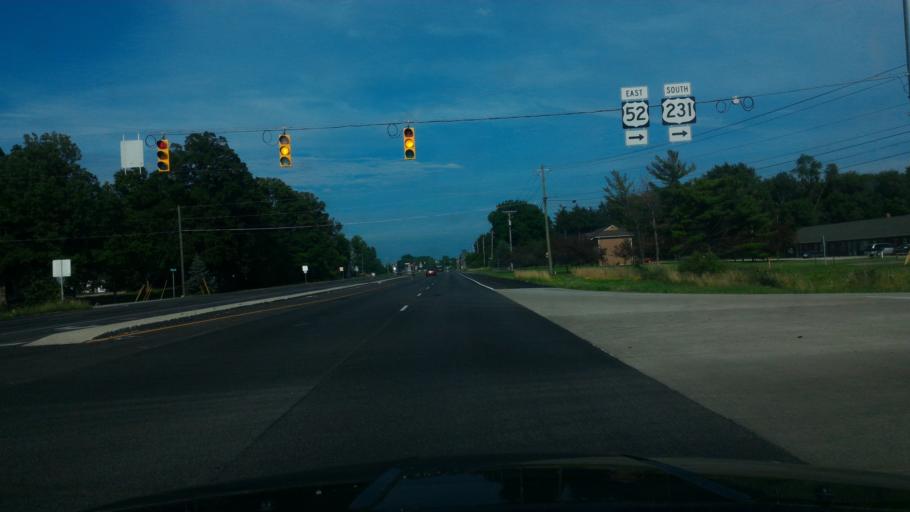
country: US
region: Indiana
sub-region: Tippecanoe County
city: West Lafayette
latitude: 40.4674
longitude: -86.9536
